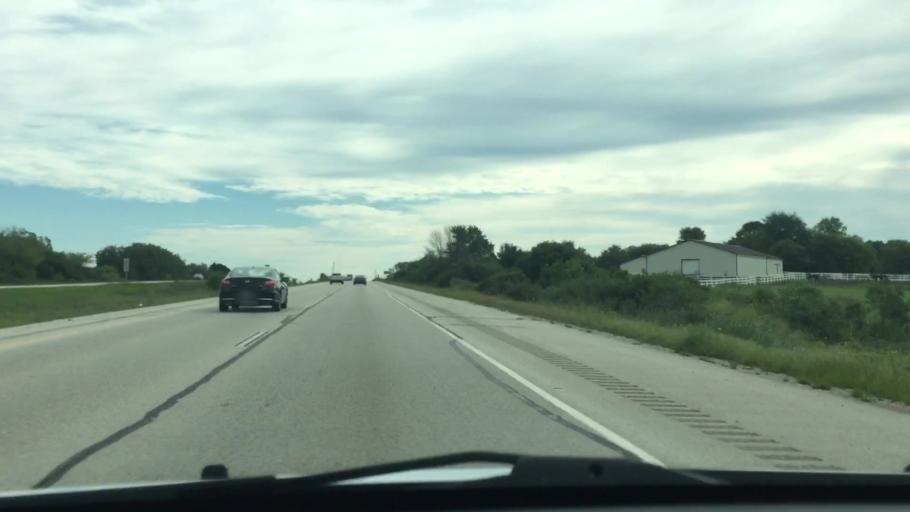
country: US
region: Wisconsin
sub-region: Waukesha County
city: Big Bend
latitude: 42.9165
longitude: -88.2026
